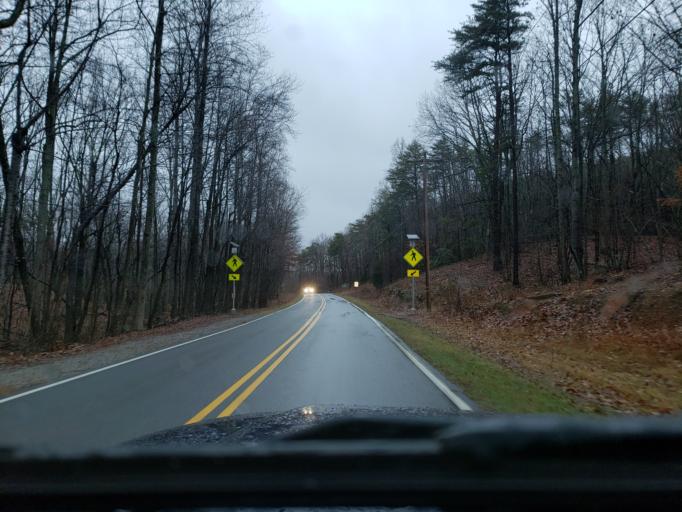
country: US
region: North Carolina
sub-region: Cleveland County
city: White Plains
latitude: 35.1731
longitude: -81.3625
